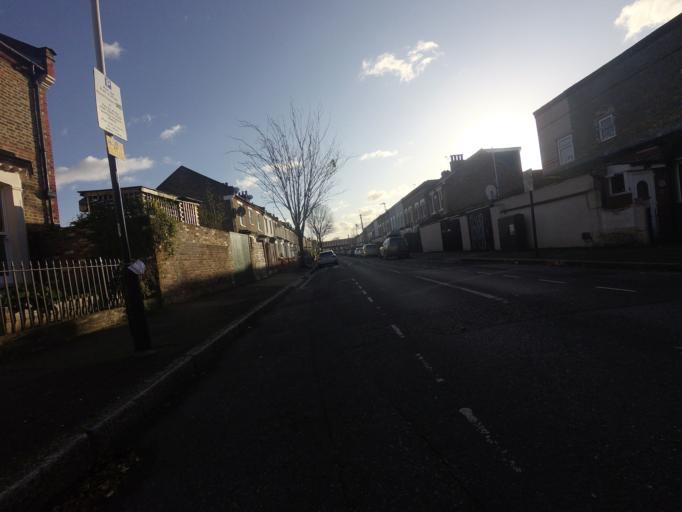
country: GB
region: England
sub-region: Greater London
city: East Ham
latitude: 51.5530
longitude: 0.0312
